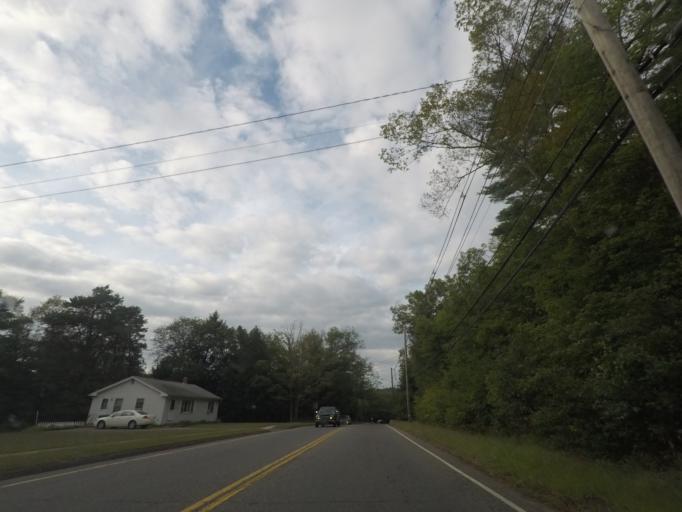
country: US
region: Massachusetts
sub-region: Hampden County
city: Palmer
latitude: 42.1708
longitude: -72.3260
